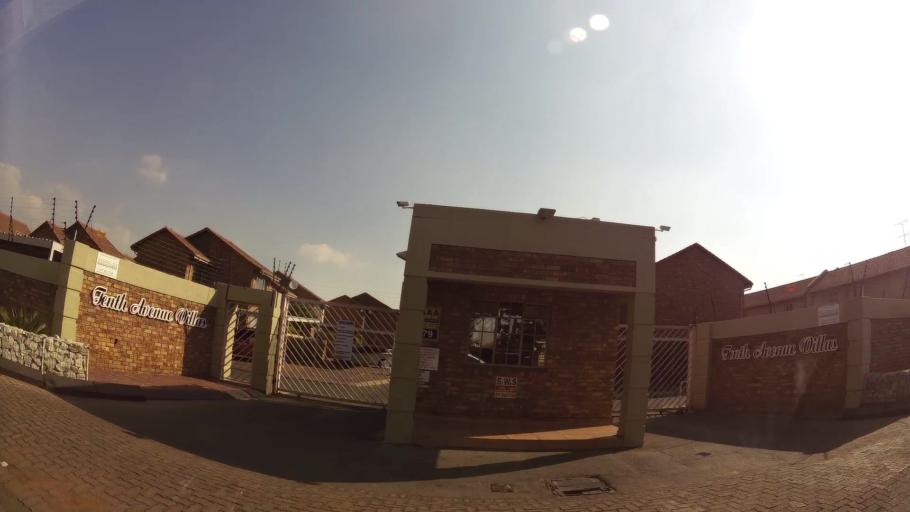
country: ZA
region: Gauteng
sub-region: Ekurhuleni Metropolitan Municipality
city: Boksburg
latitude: -26.1915
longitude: 28.2583
